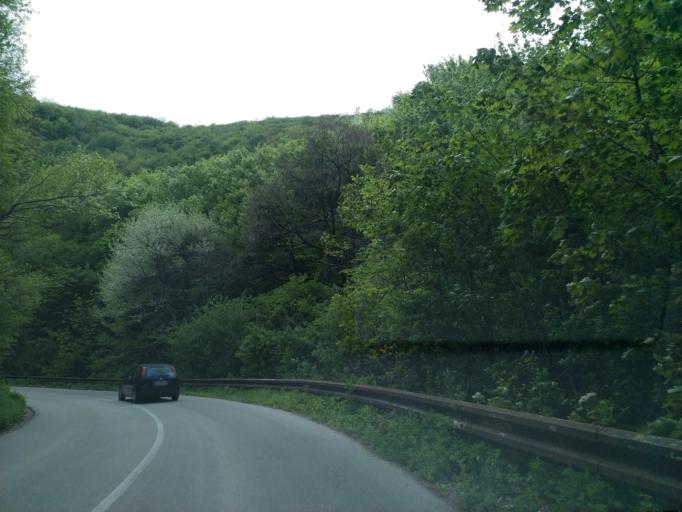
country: RS
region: Central Serbia
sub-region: Pomoravski Okrug
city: Despotovac
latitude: 43.9698
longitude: 21.5250
